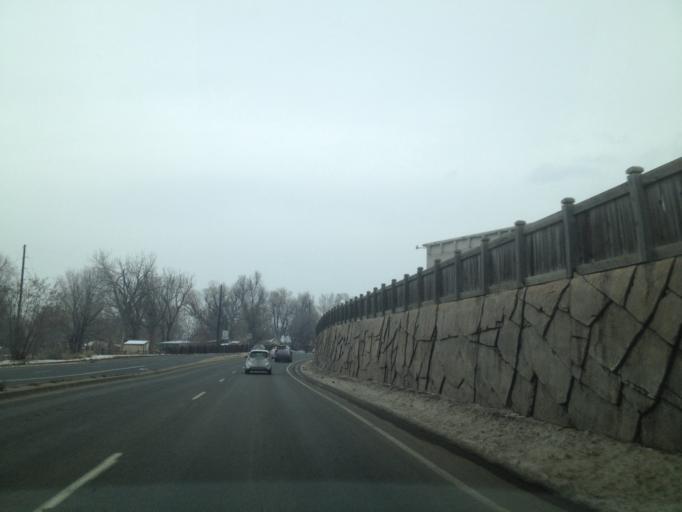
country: US
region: Colorado
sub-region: Boulder County
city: Gunbarrel
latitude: 40.0303
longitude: -105.2157
